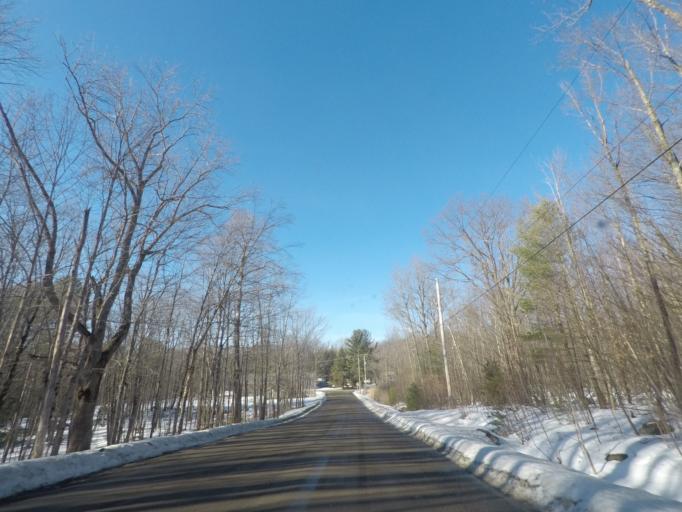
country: US
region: New York
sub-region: Rensselaer County
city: Averill Park
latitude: 42.6496
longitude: -73.5026
